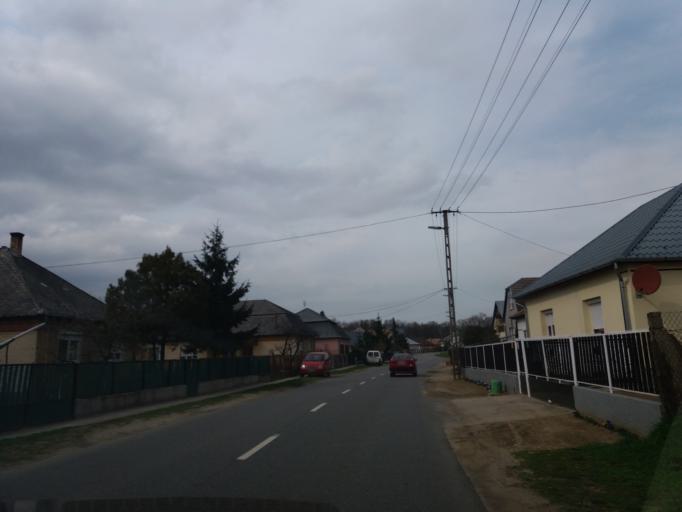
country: HU
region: Szabolcs-Szatmar-Bereg
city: Anarcs
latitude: 48.1709
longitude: 22.0968
